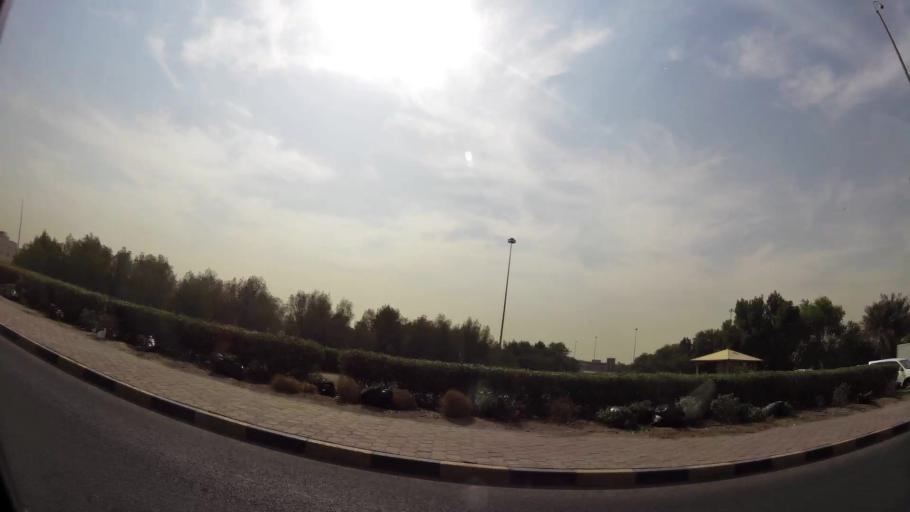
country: KW
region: Al Farwaniyah
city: Janub as Surrah
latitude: 29.2840
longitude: 47.9866
